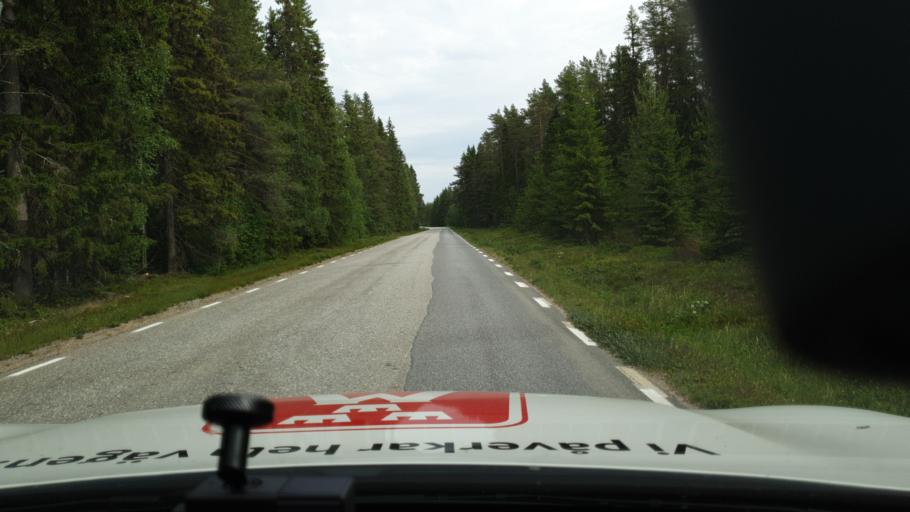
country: SE
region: Vaesterbotten
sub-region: Umea Kommun
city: Hoernefors
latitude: 63.5610
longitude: 19.7273
